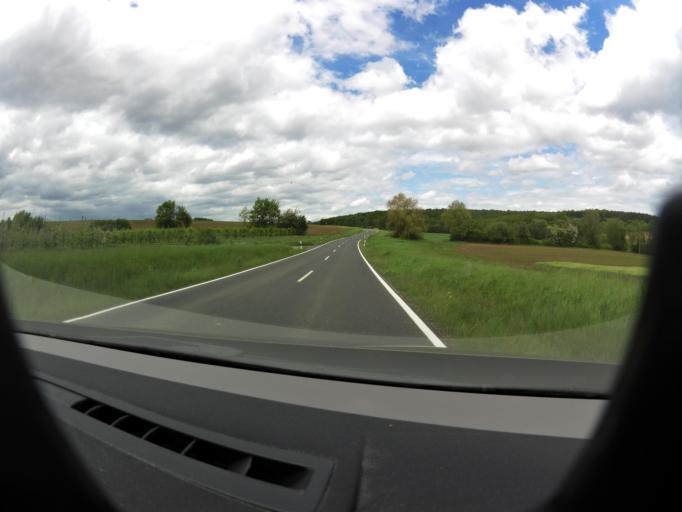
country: DE
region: Bavaria
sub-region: Regierungsbezirk Unterfranken
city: Prosselsheim
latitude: 49.8439
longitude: 10.1453
